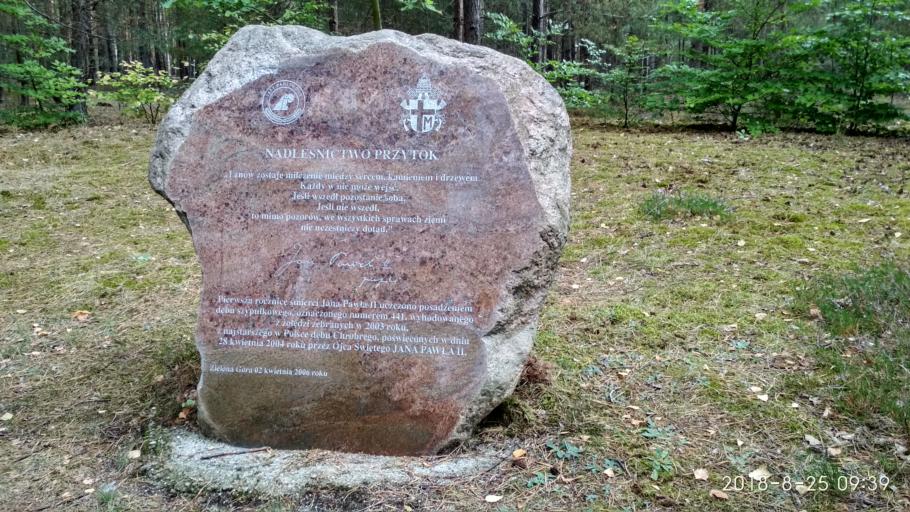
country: PL
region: Lubusz
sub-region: Zielona Gora
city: Zielona Gora
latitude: 51.9434
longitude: 15.5906
